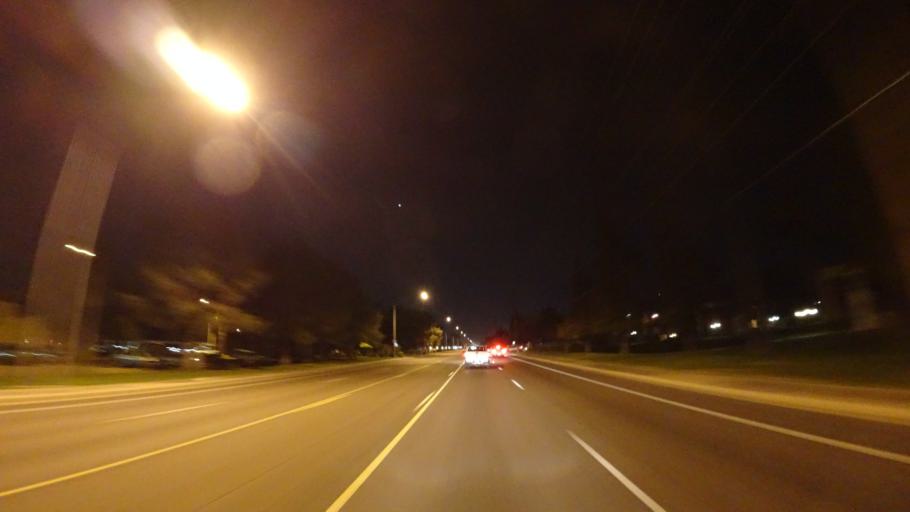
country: US
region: Arizona
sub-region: Maricopa County
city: Mesa
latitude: 33.4228
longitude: -111.7392
